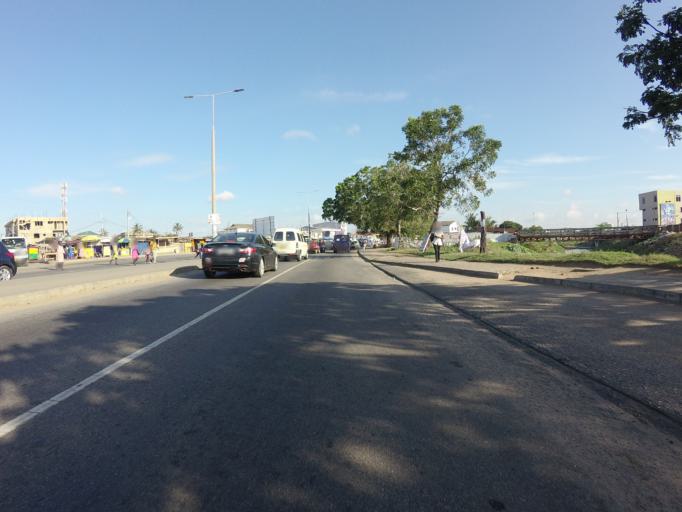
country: GH
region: Greater Accra
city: Accra
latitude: 5.5539
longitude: -0.2313
